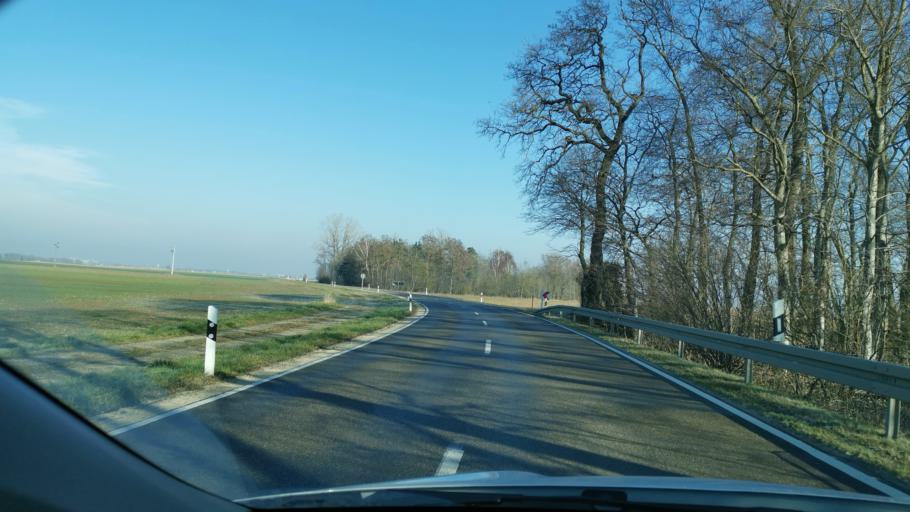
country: DE
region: Bavaria
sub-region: Swabia
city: Munster
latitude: 48.6441
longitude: 10.9210
